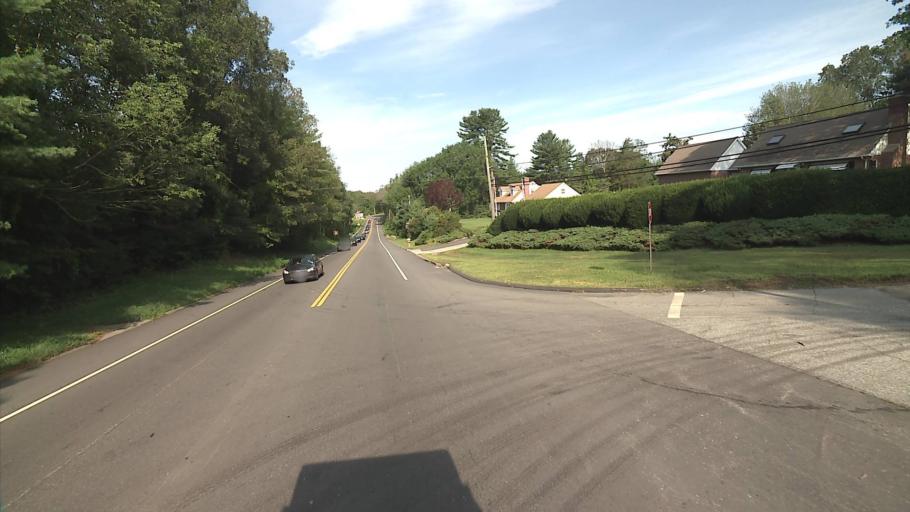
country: US
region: Connecticut
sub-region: New London County
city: Ledyard Center
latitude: 41.4930
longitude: -72.0207
